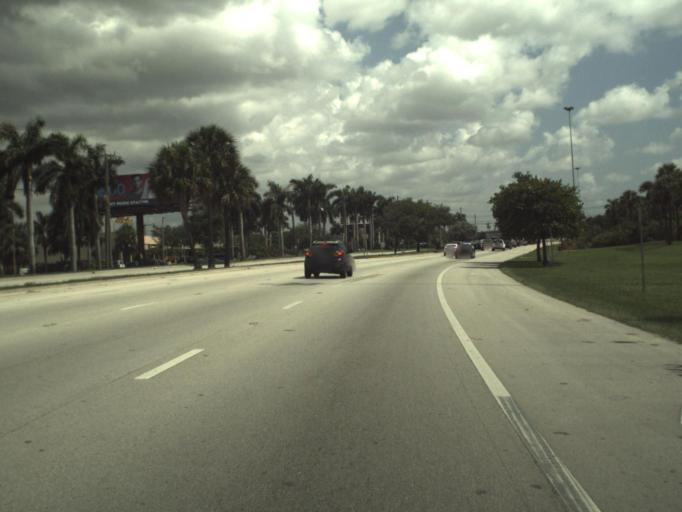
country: US
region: Florida
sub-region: Broward County
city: Davie
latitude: 26.0675
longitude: -80.2079
